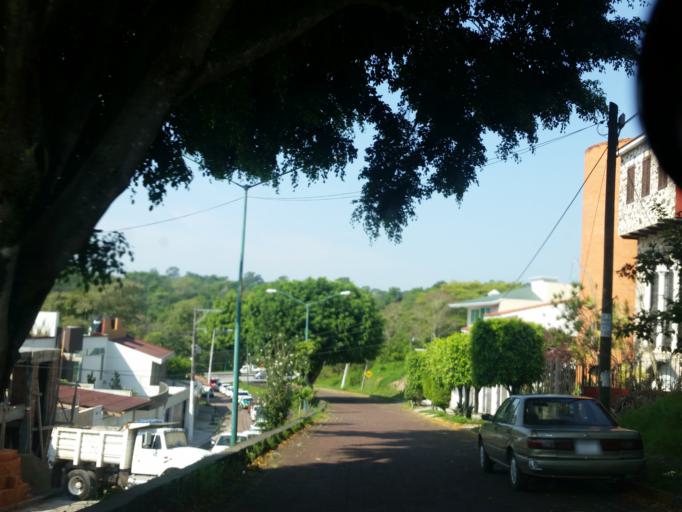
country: MX
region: Veracruz
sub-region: Xalapa
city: Xalapa de Enriquez
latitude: 19.5203
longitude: -96.9029
